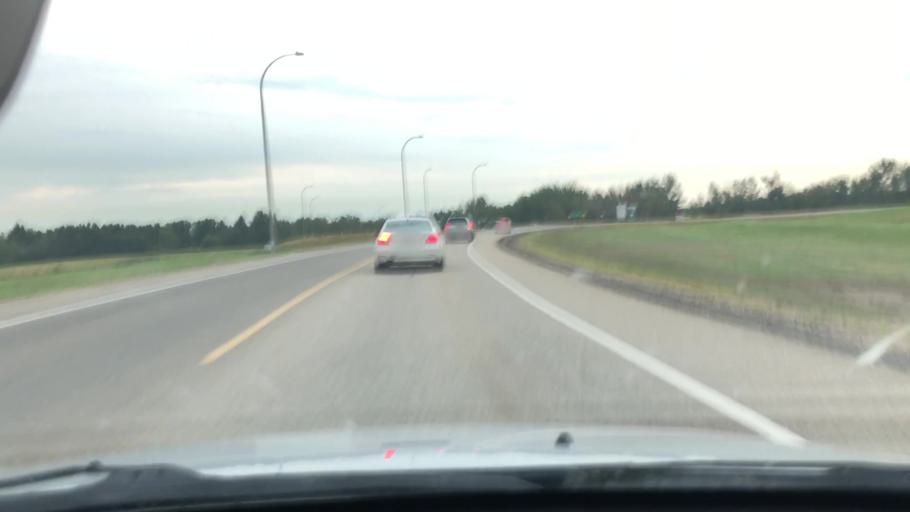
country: CA
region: Alberta
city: Devon
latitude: 53.4613
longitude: -113.6374
